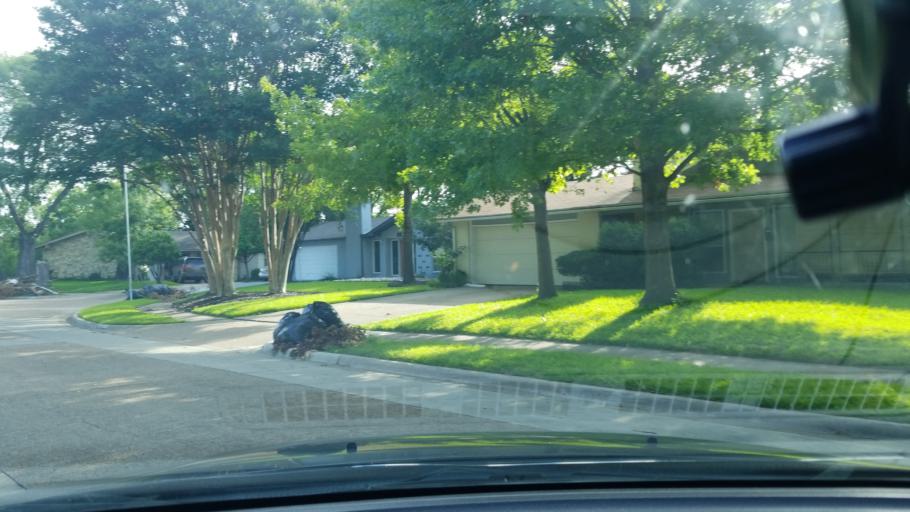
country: US
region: Texas
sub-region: Dallas County
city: Mesquite
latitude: 32.8158
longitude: -96.6851
